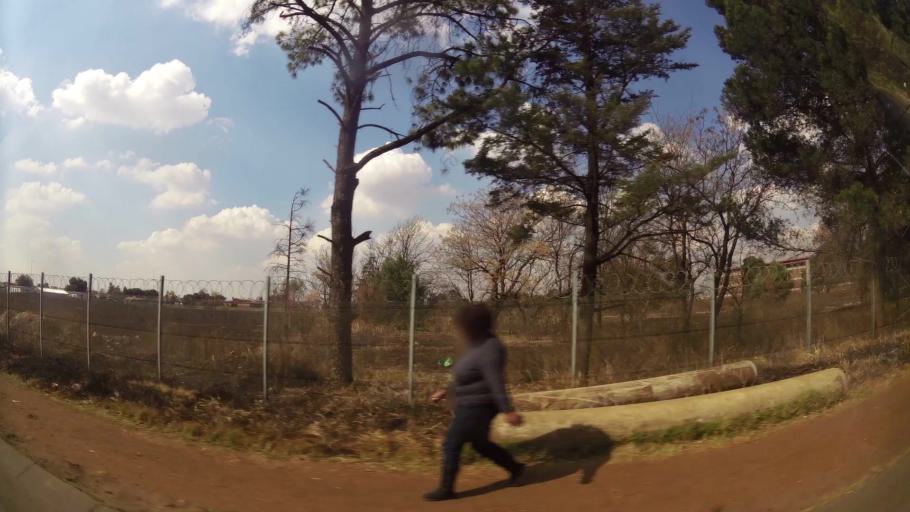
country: ZA
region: Gauteng
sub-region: Ekurhuleni Metropolitan Municipality
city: Germiston
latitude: -26.3229
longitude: 28.1423
